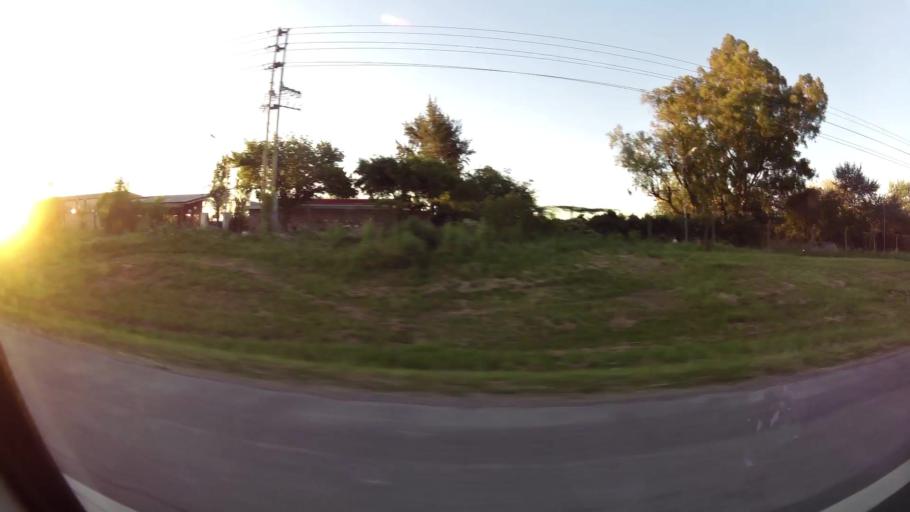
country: AR
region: Buenos Aires
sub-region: Partido de Quilmes
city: Quilmes
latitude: -34.8065
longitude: -58.1710
